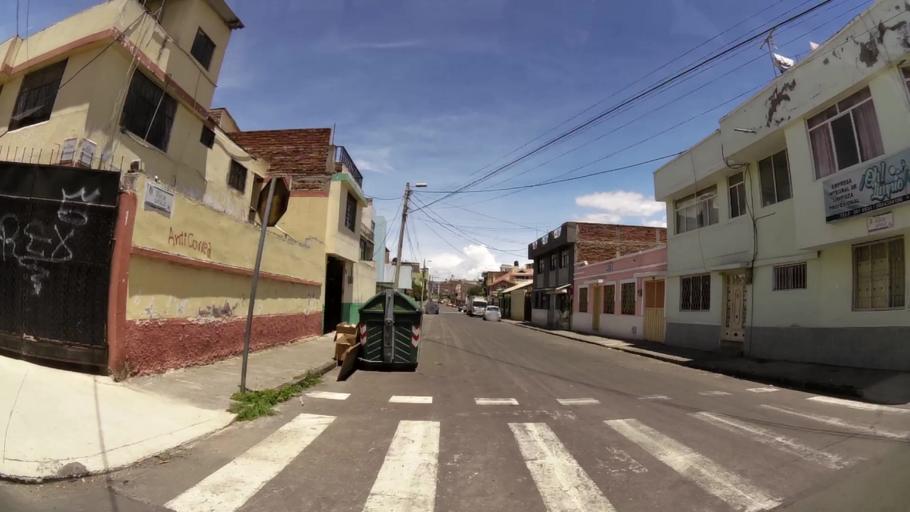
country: EC
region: Chimborazo
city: Riobamba
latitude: -1.6654
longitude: -78.6514
